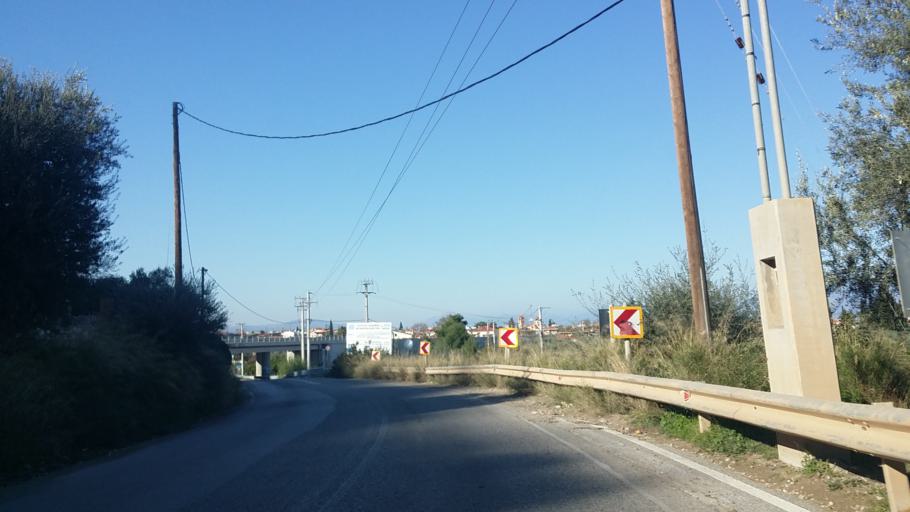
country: GR
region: West Greece
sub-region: Nomos Achaias
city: Temeni
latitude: 38.1821
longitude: 22.2090
